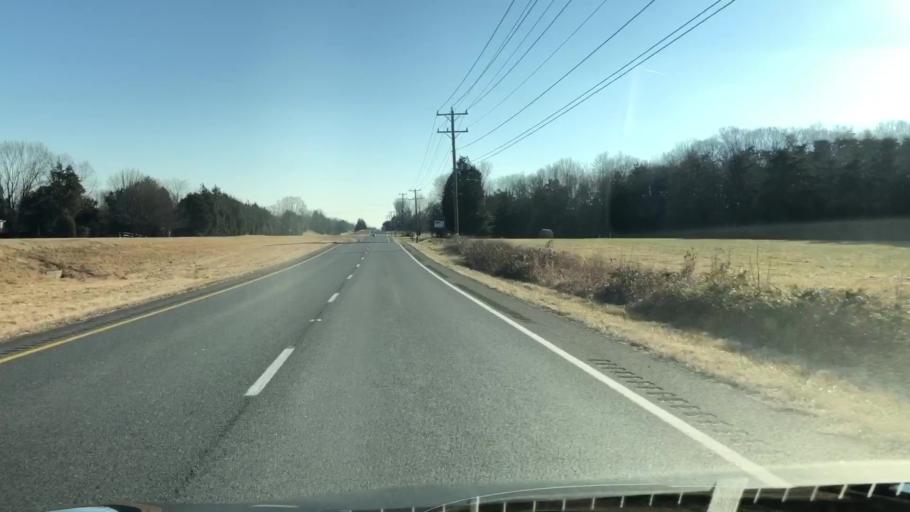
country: US
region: Virginia
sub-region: Fauquier County
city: Bealeton
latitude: 38.5748
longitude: -77.8019
